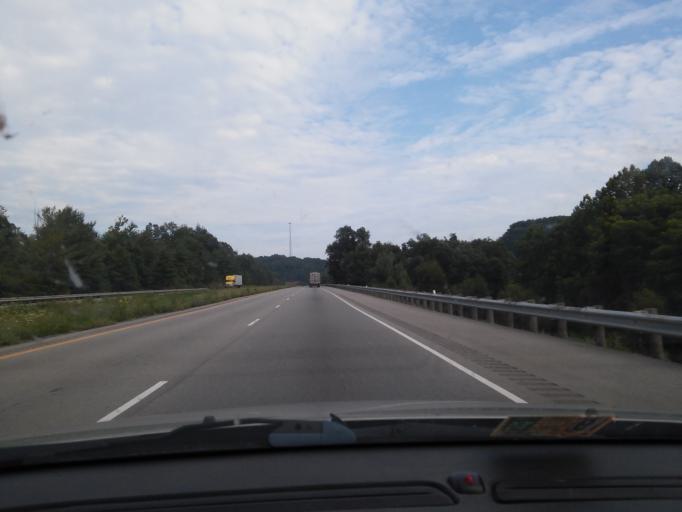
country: US
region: Ohio
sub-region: Jackson County
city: Jackson
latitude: 39.1855
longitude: -82.7580
